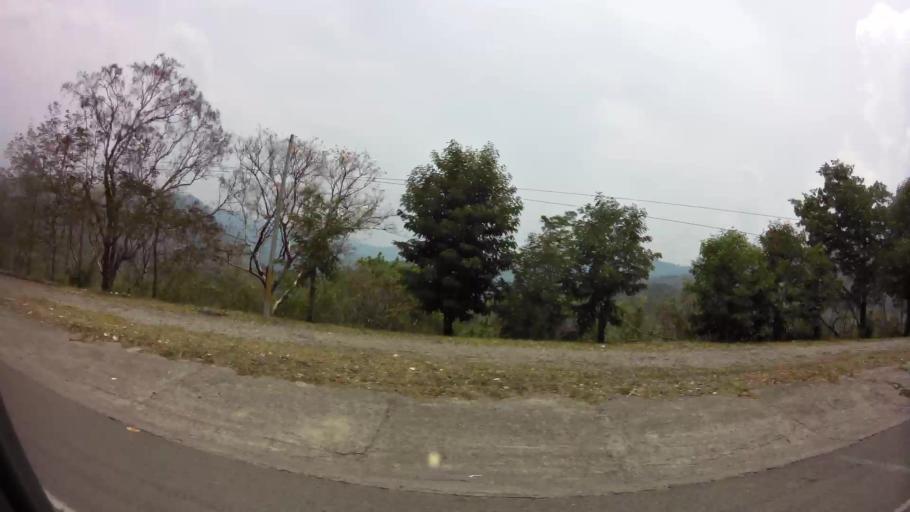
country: HN
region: Comayagua
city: Taulabe
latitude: 14.6951
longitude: -87.9541
